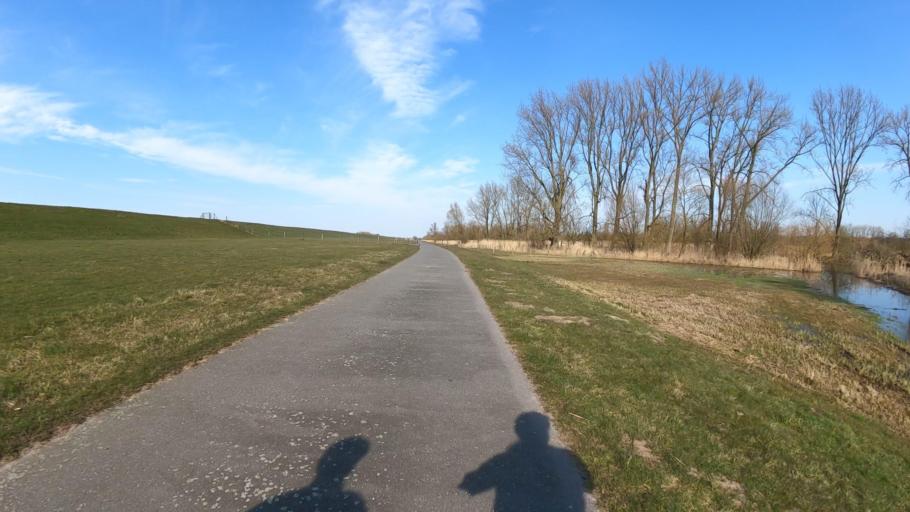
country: DE
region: Schleswig-Holstein
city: Haseldorf
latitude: 53.6230
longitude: 9.5820
